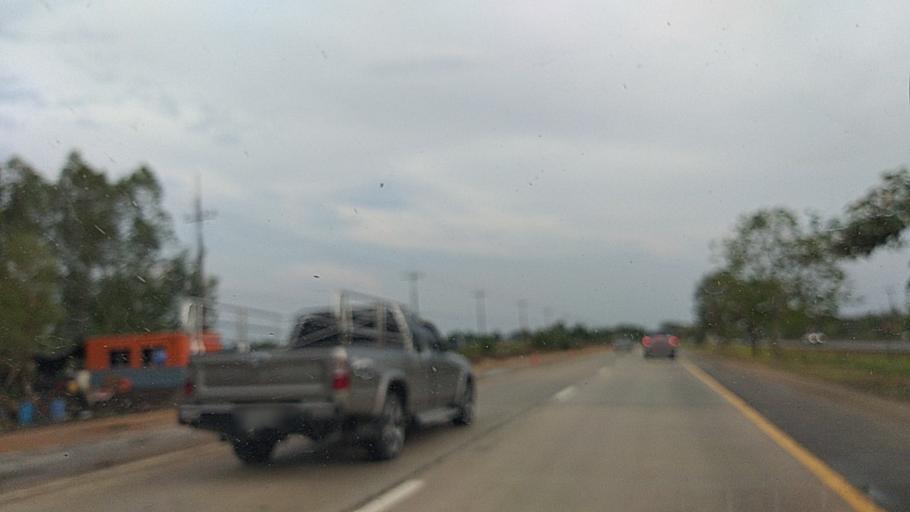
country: TH
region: Phra Nakhon Si Ayutthaya
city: Bang Pa-in
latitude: 14.2370
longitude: 100.5386
